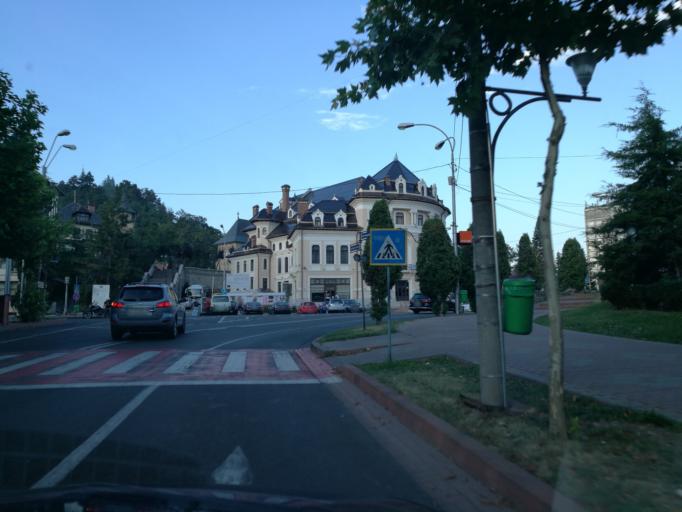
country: RO
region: Neamt
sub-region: Municipiul Piatra-Neamt
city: Valeni
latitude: 46.9318
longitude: 26.3672
